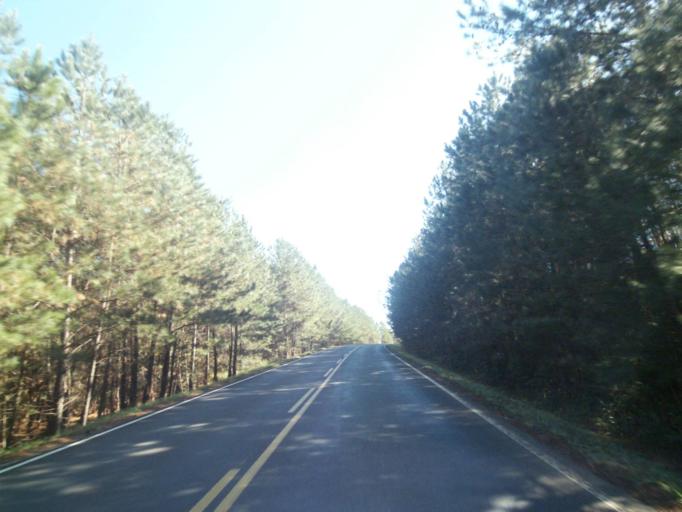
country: BR
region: Parana
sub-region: Telemaco Borba
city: Telemaco Borba
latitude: -24.4494
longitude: -50.5471
